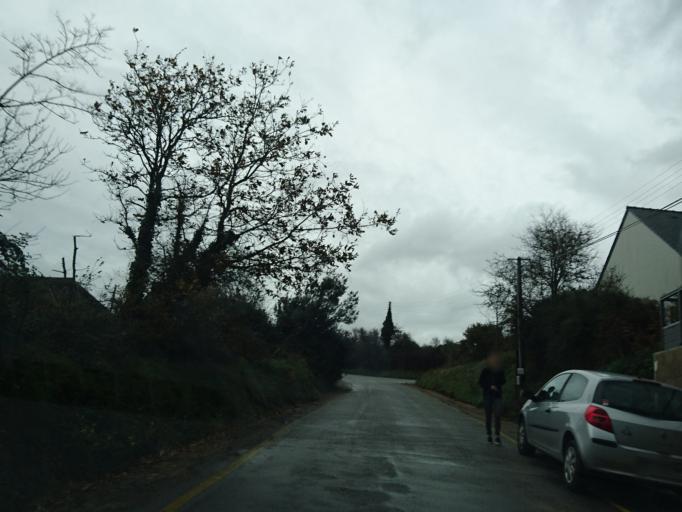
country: FR
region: Brittany
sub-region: Departement du Finistere
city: Plougonvelin
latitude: 48.3580
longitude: -4.6776
